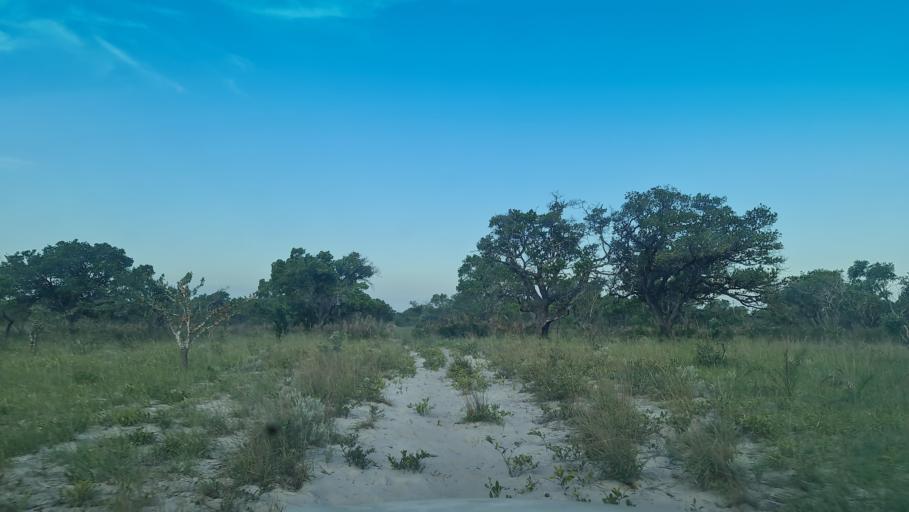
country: MZ
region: Gaza
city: Macia
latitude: -25.2158
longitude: 33.0505
